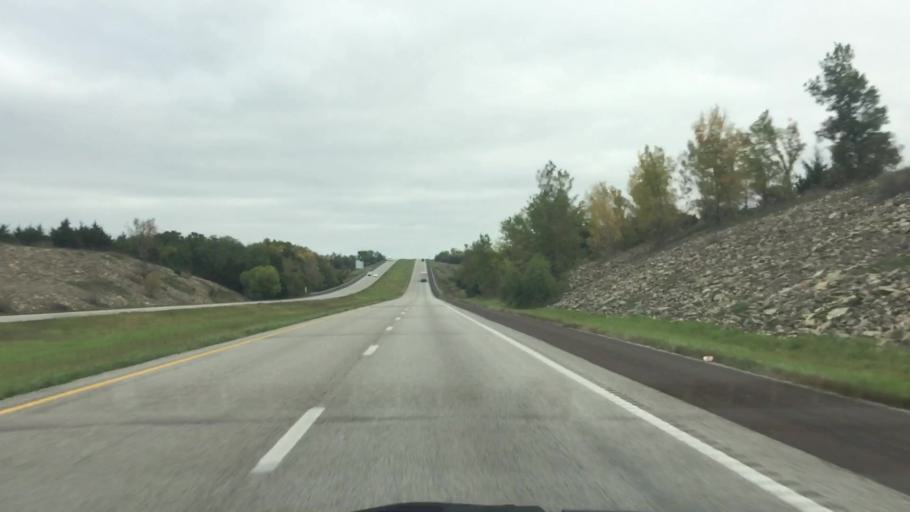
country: US
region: Missouri
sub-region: Daviess County
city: Gallatin
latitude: 39.9114
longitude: -94.1450
